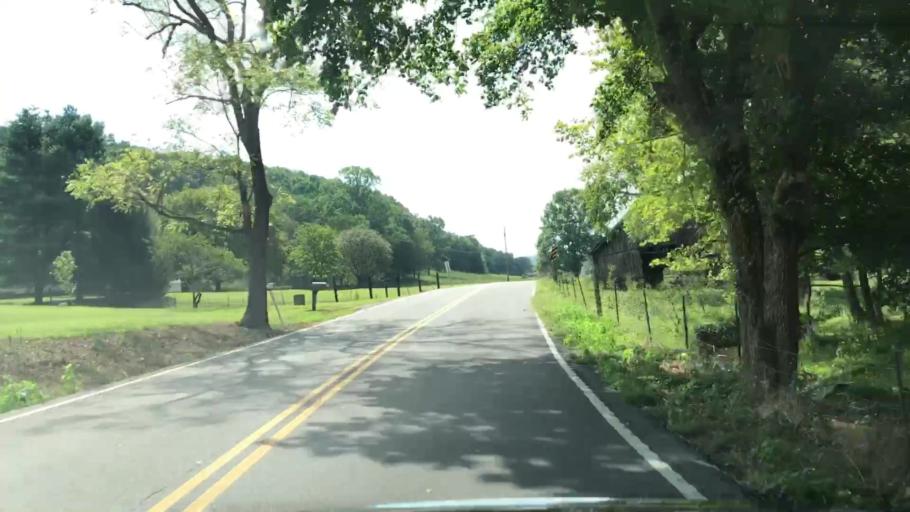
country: US
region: Tennessee
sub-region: Trousdale County
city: Hartsville
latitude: 36.4855
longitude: -86.1884
